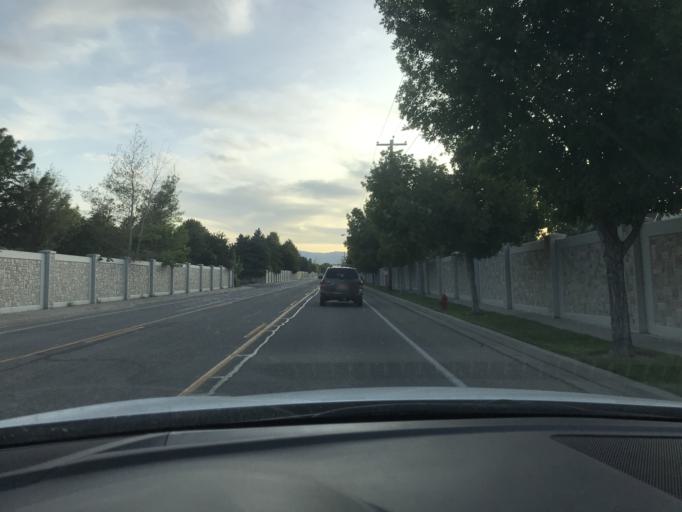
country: US
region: Utah
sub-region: Salt Lake County
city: South Jordan Heights
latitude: 40.5733
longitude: -111.9519
